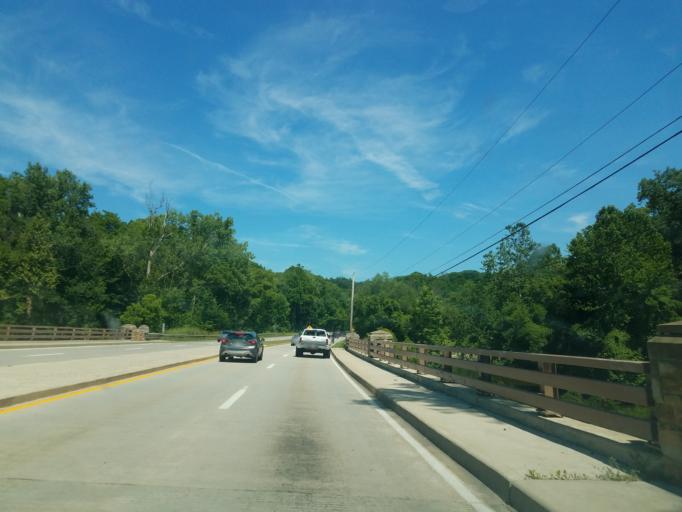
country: US
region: Ohio
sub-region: Cuyahoga County
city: Gates Mills
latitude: 41.5295
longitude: -81.4134
